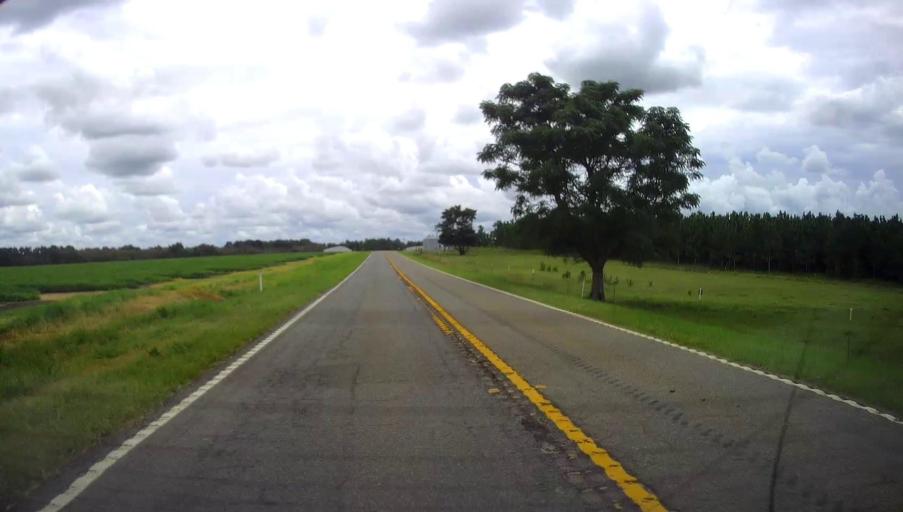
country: US
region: Georgia
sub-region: Dooly County
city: Unadilla
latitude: 32.2621
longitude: -83.8080
